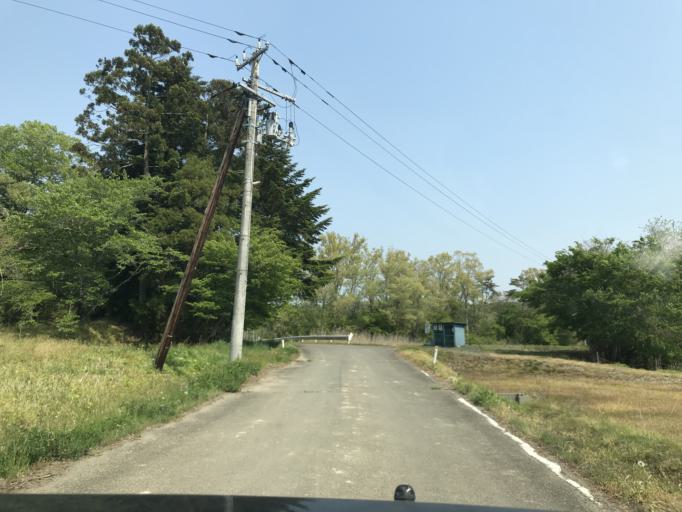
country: JP
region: Iwate
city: Ichinoseki
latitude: 38.8579
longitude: 141.0651
